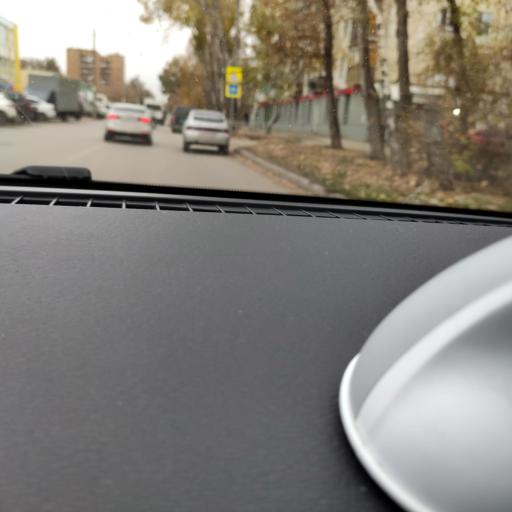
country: RU
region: Samara
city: Samara
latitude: 53.1878
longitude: 50.1744
